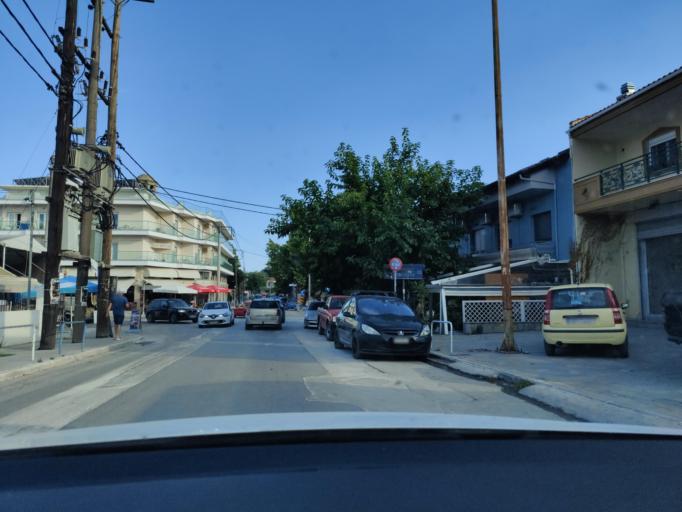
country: GR
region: East Macedonia and Thrace
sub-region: Nomos Kavalas
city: Limenaria
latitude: 40.6107
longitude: 24.6072
